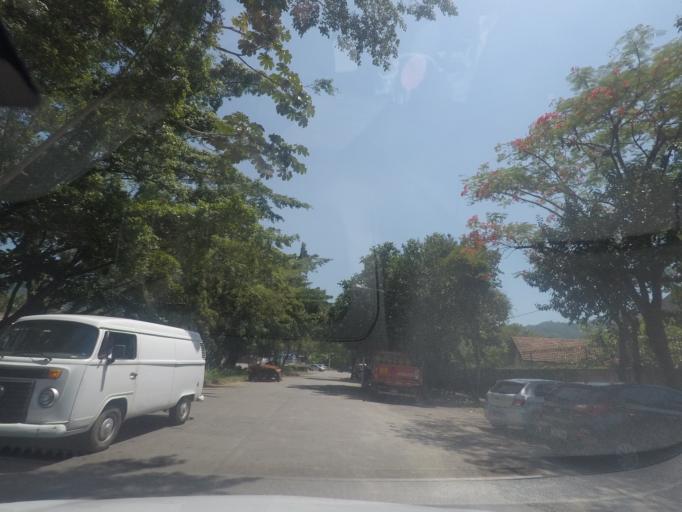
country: BR
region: Rio de Janeiro
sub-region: Nilopolis
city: Nilopolis
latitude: -22.9889
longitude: -43.4553
